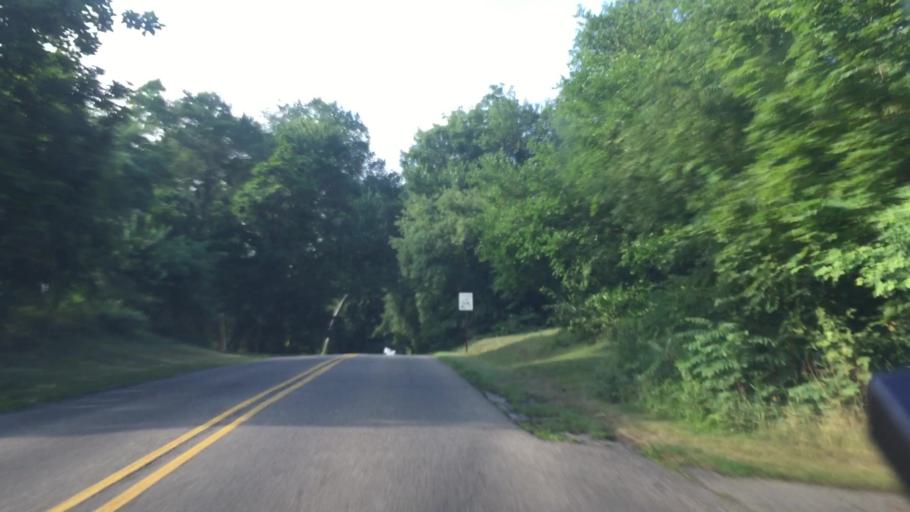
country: US
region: Michigan
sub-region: Oakland County
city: Bloomfield Hills
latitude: 42.5917
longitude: -83.2474
